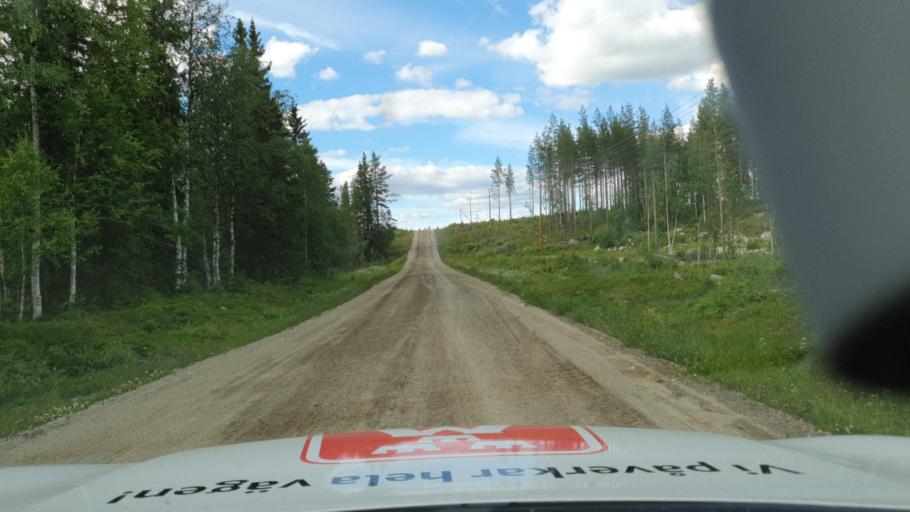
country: SE
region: Vaesterbotten
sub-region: Lycksele Kommun
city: Lycksele
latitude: 64.3003
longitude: 18.2883
